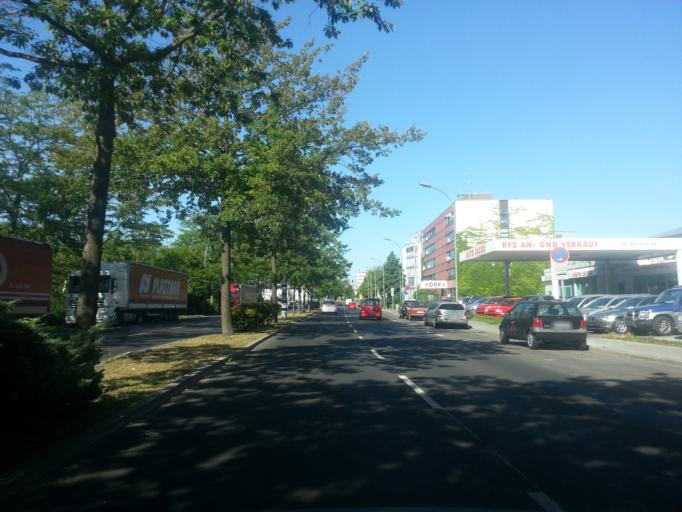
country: DE
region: Hesse
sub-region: Regierungsbezirk Darmstadt
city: Offenbach
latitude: 50.0905
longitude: 8.7755
